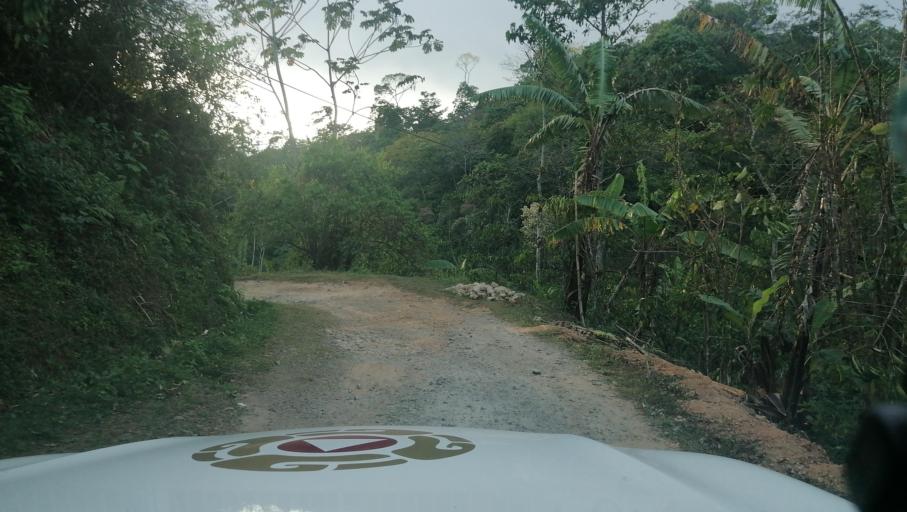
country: MX
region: Chiapas
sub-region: Cacahoatan
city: Benito Juarez
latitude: 15.1001
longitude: -92.2206
